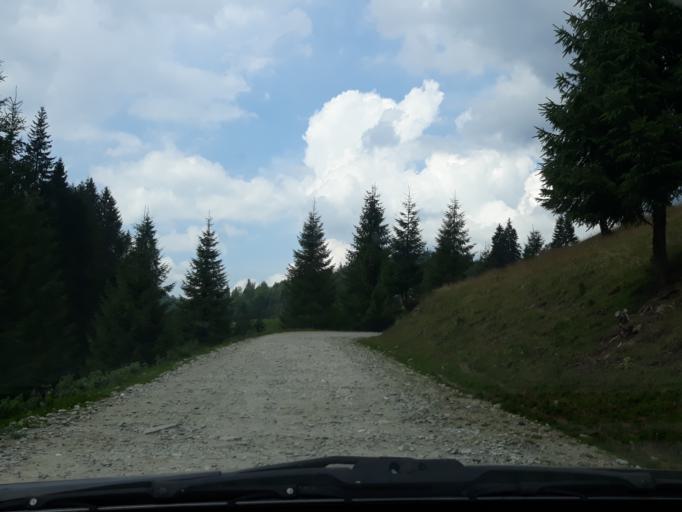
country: RO
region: Alba
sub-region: Comuna Arieseni
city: Arieseni
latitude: 46.5848
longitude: 22.6977
